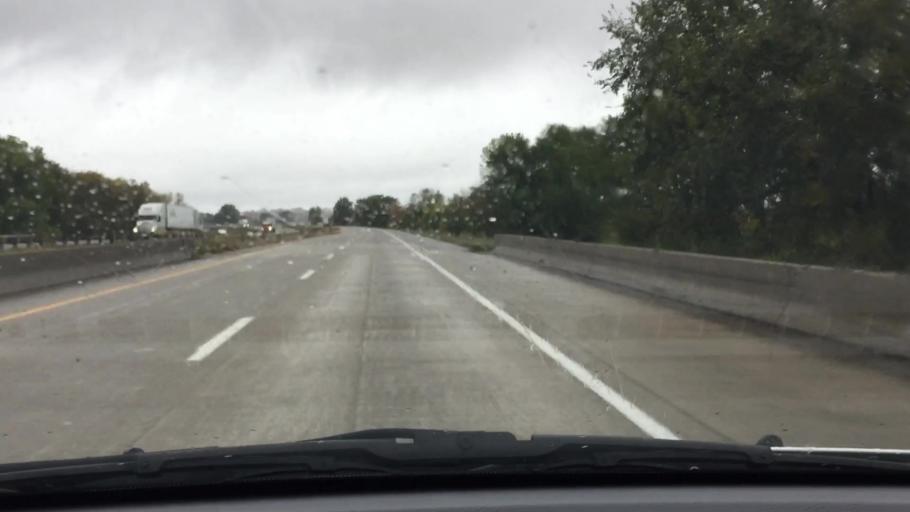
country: US
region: Iowa
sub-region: Jasper County
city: Colfax
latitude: 41.6979
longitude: -93.1984
